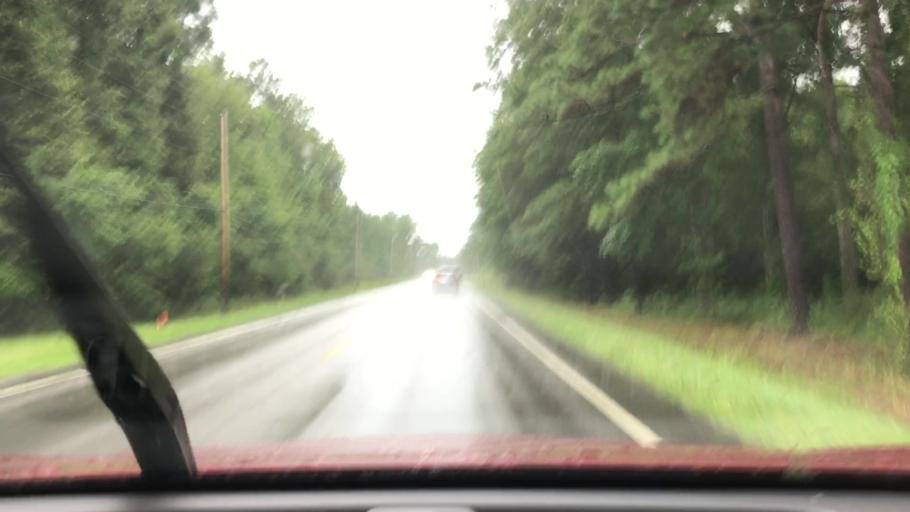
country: US
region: South Carolina
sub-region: Horry County
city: Conway
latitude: 33.7874
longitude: -79.0756
